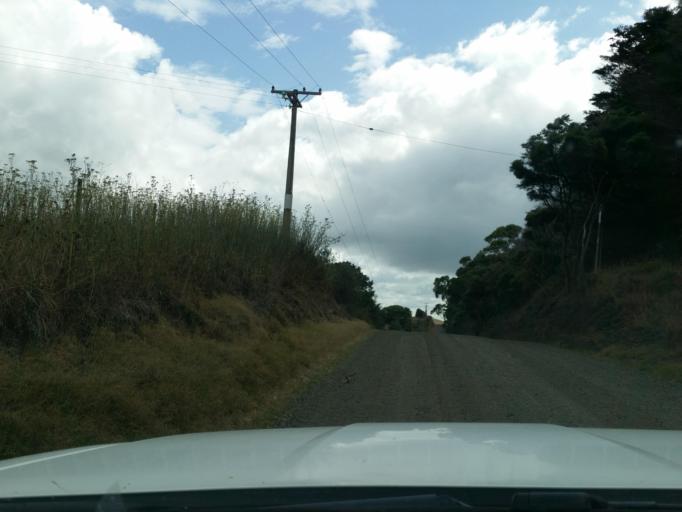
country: NZ
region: Auckland
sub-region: Auckland
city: Wellsford
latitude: -36.3570
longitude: 174.1756
